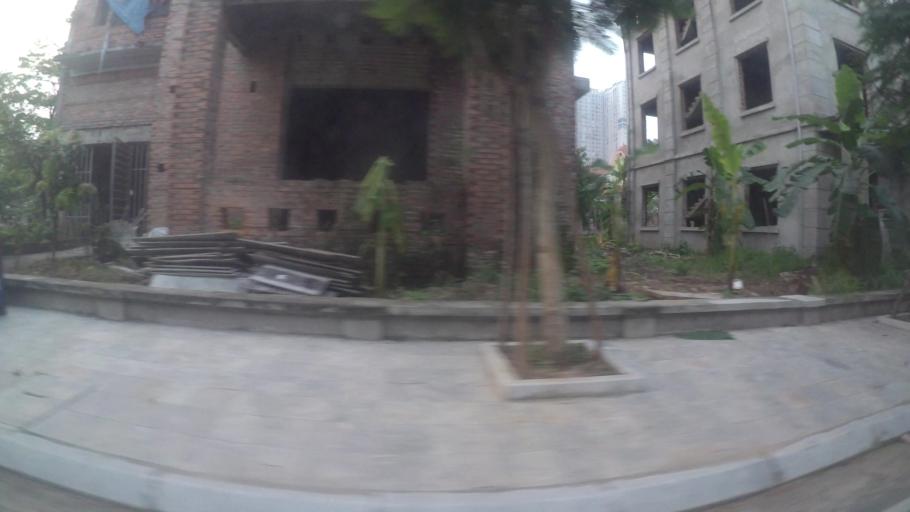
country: VN
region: Ha Noi
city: Cau Dien
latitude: 20.9999
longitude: 105.7318
